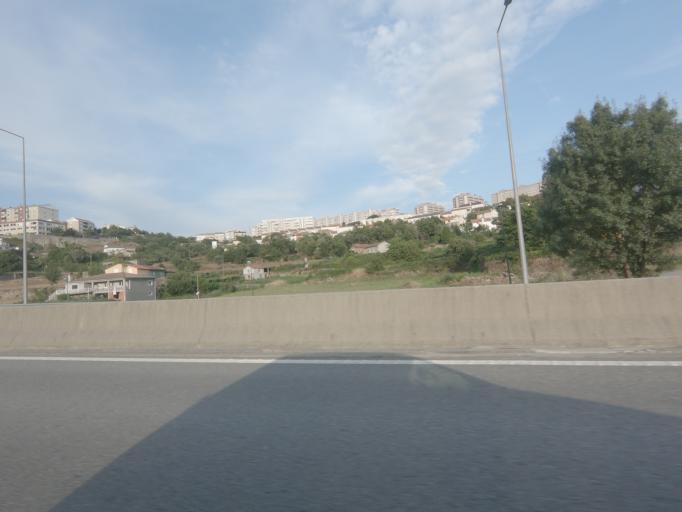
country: PT
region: Vila Real
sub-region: Vila Real
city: Vila Real
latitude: 41.3090
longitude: -7.7500
